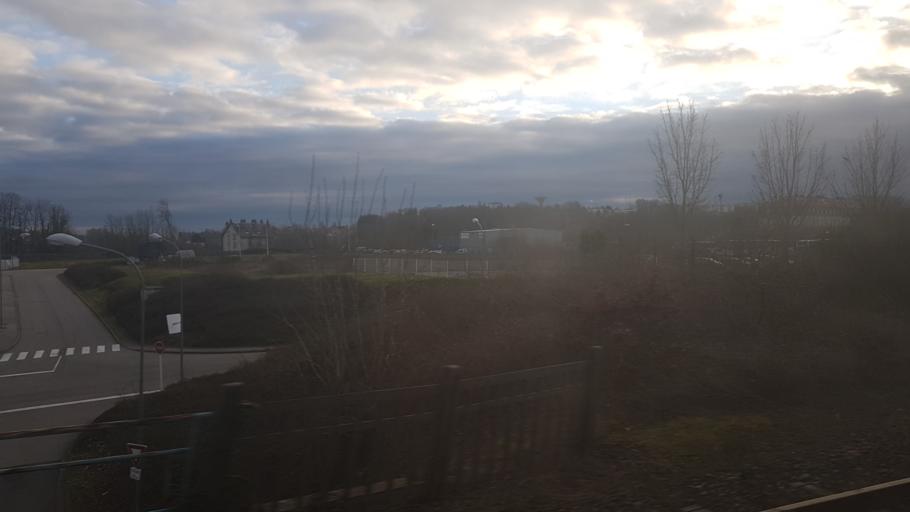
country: FR
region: Lorraine
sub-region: Departement des Vosges
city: Golbey
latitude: 48.1906
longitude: 6.4373
